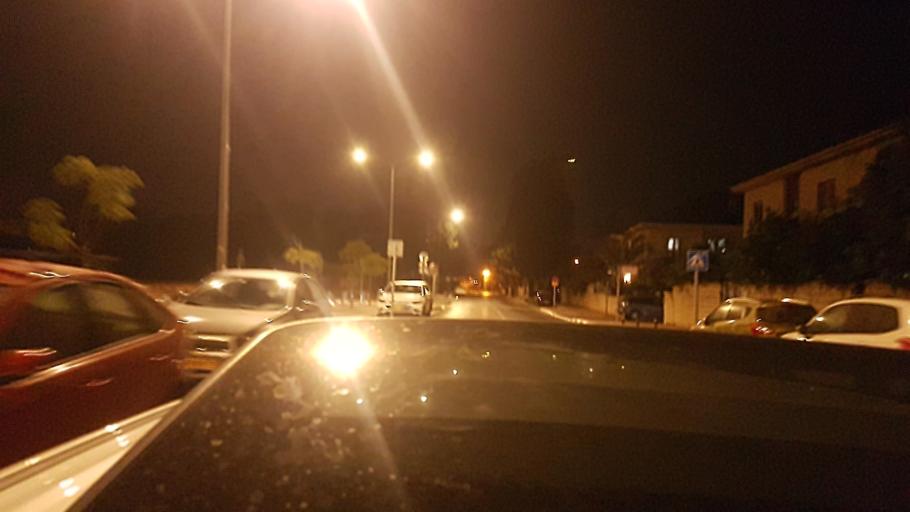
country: IL
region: Central District
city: Hod HaSharon
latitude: 32.1607
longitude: 34.8868
